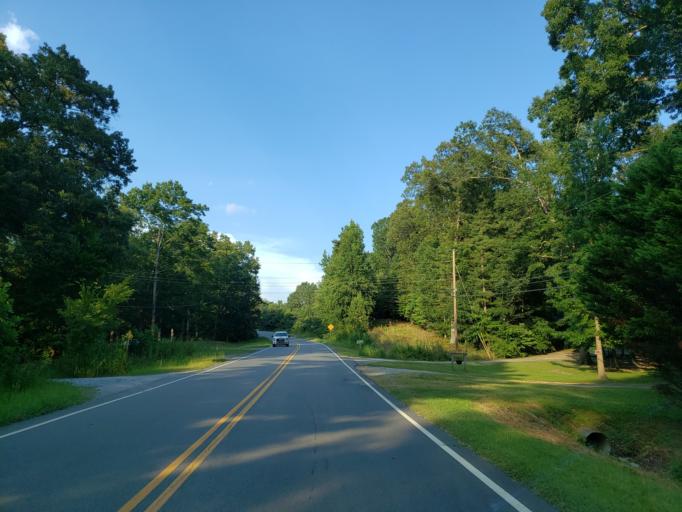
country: US
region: Georgia
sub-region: Polk County
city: Rockmart
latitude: 33.9738
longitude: -85.0082
